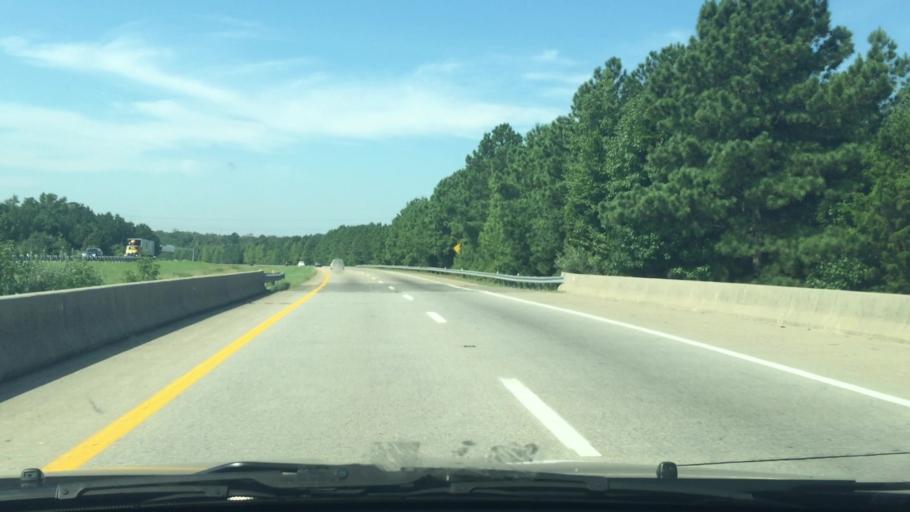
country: US
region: Virginia
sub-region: Prince George County
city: Prince George
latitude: 37.1908
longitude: -77.3319
